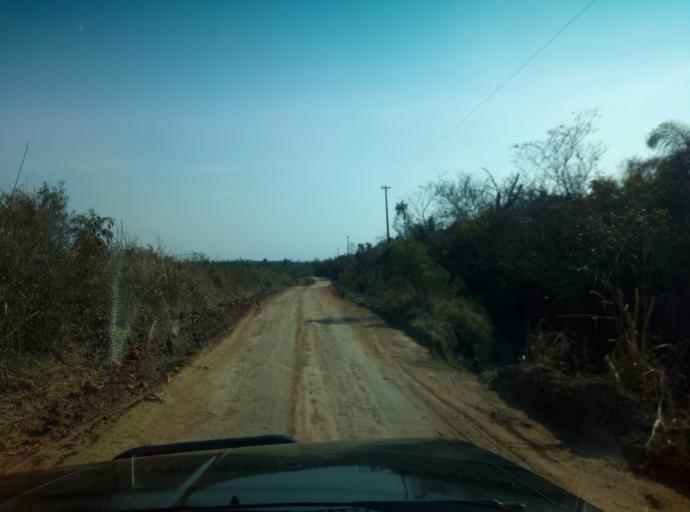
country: PY
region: Caaguazu
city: Doctor Cecilio Baez
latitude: -25.1894
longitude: -56.1918
